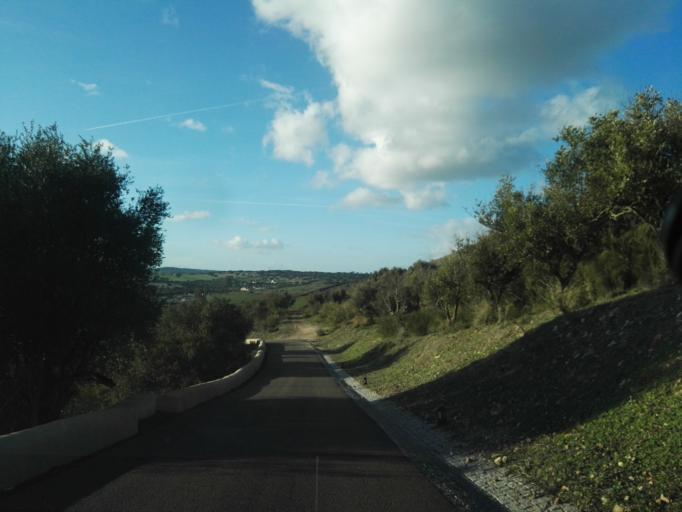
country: PT
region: Portalegre
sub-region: Elvas
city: Elvas
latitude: 38.8932
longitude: -7.1660
